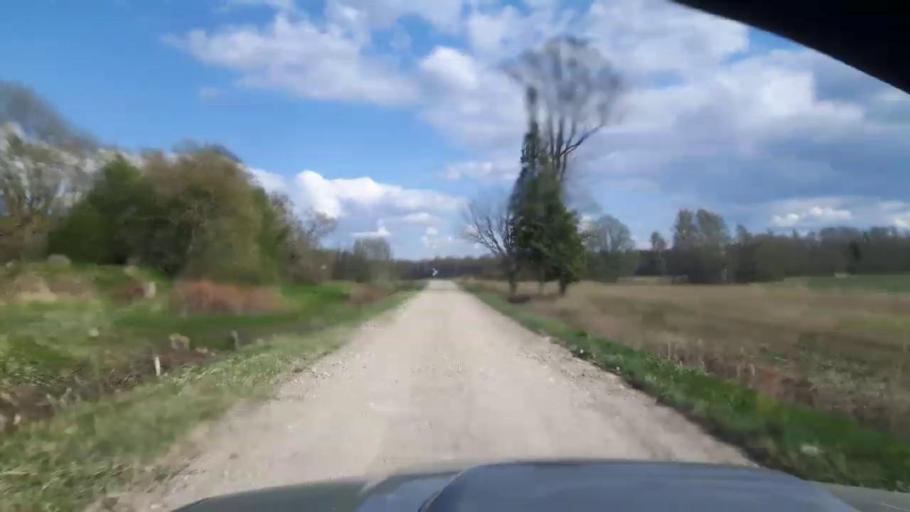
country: EE
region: Paernumaa
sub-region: Tootsi vald
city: Tootsi
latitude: 58.4353
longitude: 24.8609
